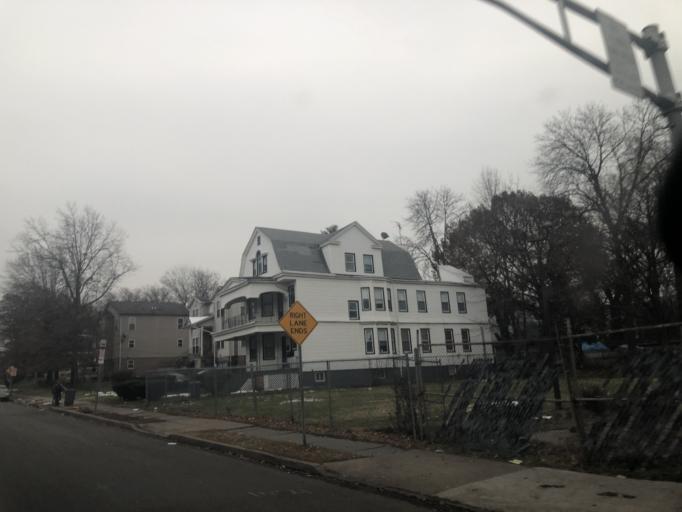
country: US
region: New Jersey
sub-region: Essex County
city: East Orange
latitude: 40.7689
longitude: -74.2096
